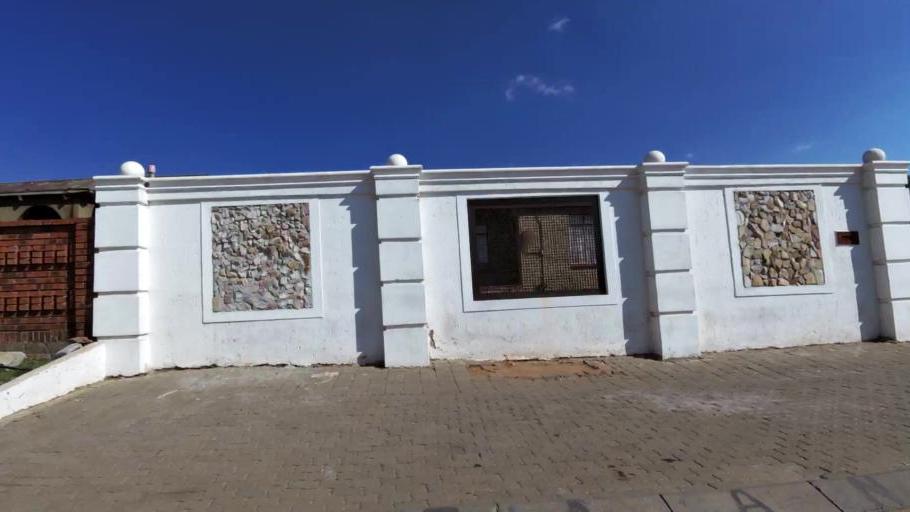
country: ZA
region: Gauteng
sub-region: City of Johannesburg Metropolitan Municipality
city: Soweto
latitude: -26.2305
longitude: 27.9102
